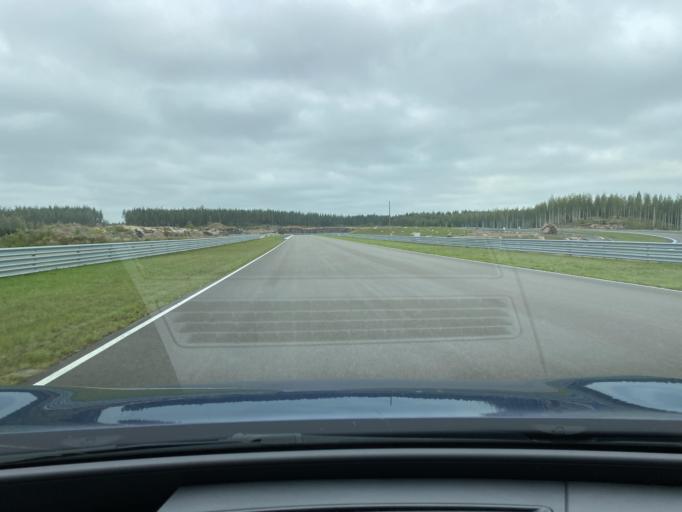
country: FI
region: Kymenlaakso
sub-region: Kouvola
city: Iitti
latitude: 60.8795
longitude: 26.4757
